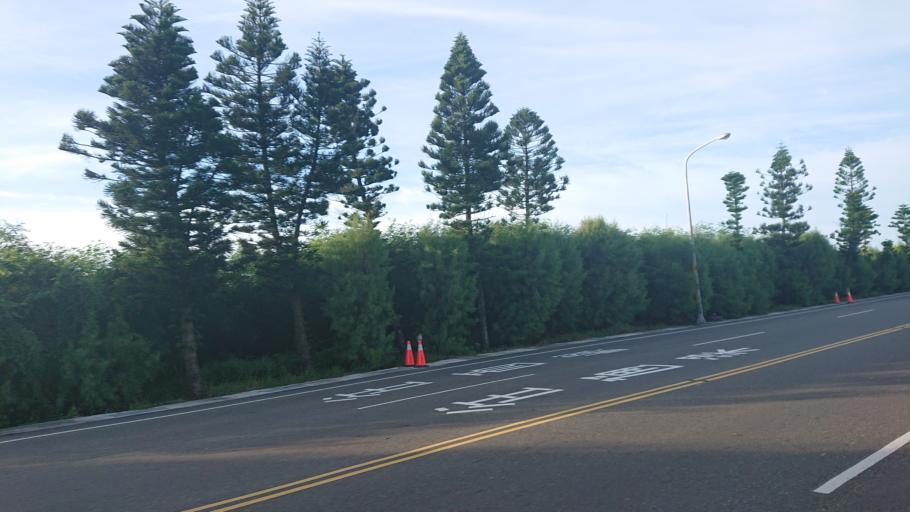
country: TW
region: Taiwan
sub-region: Penghu
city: Ma-kung
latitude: 23.6603
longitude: 119.5654
